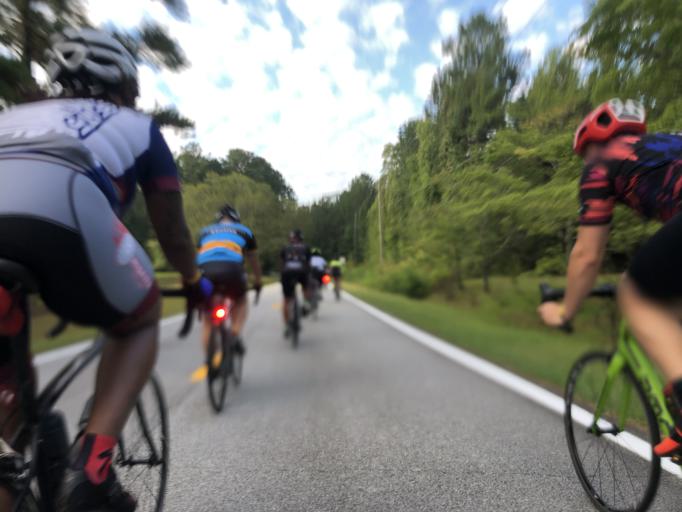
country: US
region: Georgia
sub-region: Fulton County
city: Fairburn
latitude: 33.5980
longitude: -84.6536
